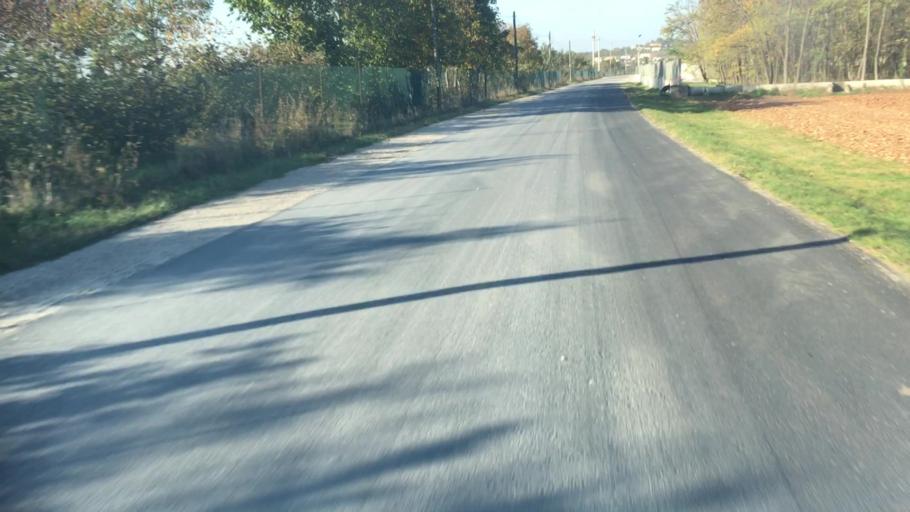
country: IT
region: Lombardy
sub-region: Provincia di Mantova
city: Guidizzolo
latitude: 45.3245
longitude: 10.5999
